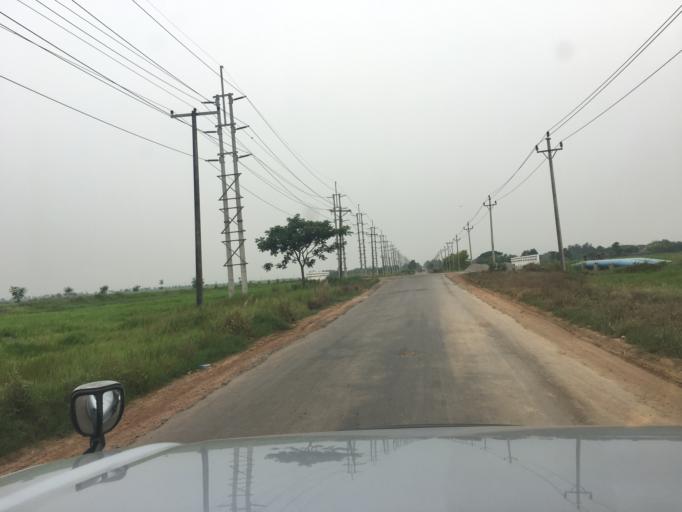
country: MM
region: Yangon
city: Yangon
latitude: 16.9555
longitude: 96.2681
